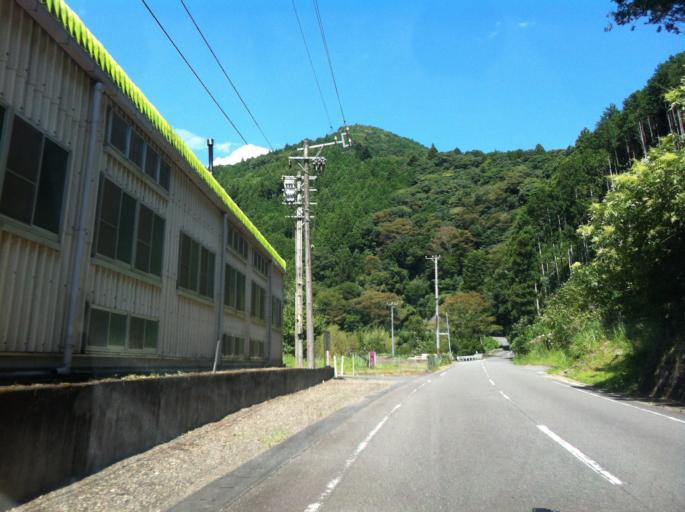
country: JP
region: Shizuoka
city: Shizuoka-shi
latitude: 35.0976
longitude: 138.2359
